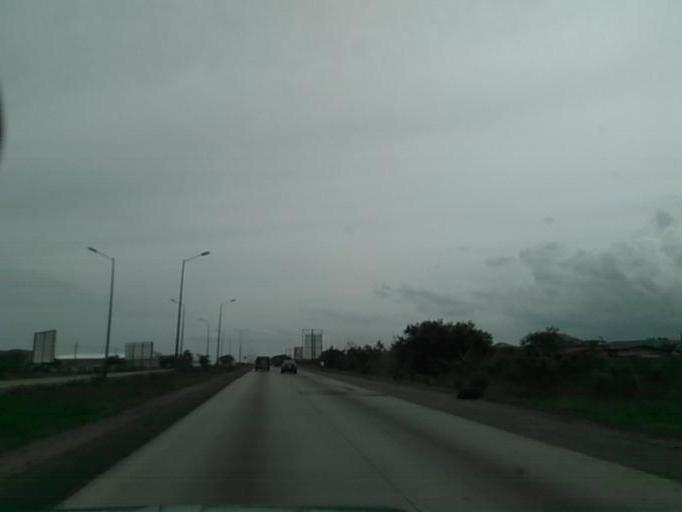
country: GH
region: Greater Accra
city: Medina Estates
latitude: 5.6424
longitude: -0.1250
